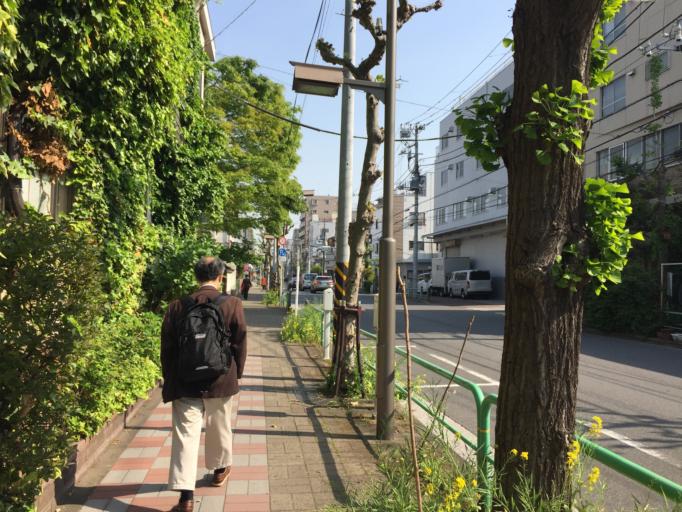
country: JP
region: Tokyo
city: Urayasu
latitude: 35.6804
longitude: 139.8038
